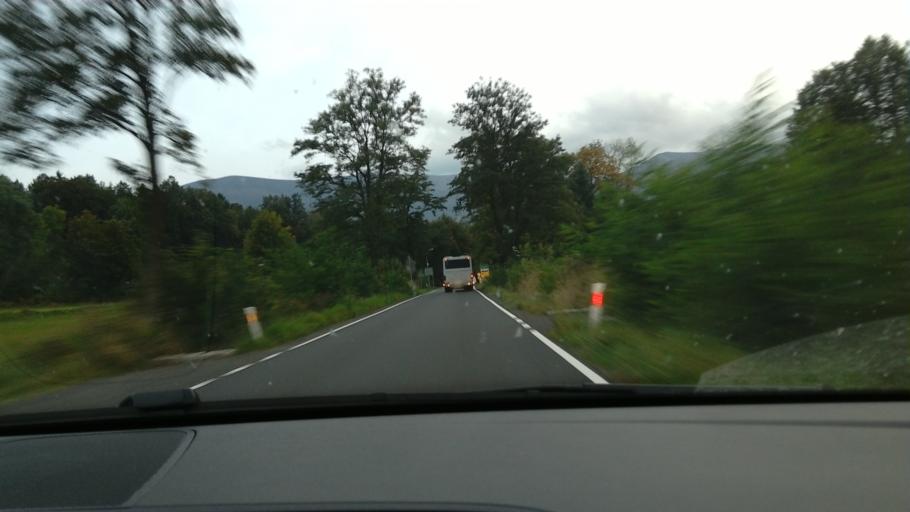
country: PL
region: Lower Silesian Voivodeship
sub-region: Powiat jeleniogorski
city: Karpacz
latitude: 50.7850
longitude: 15.7665
